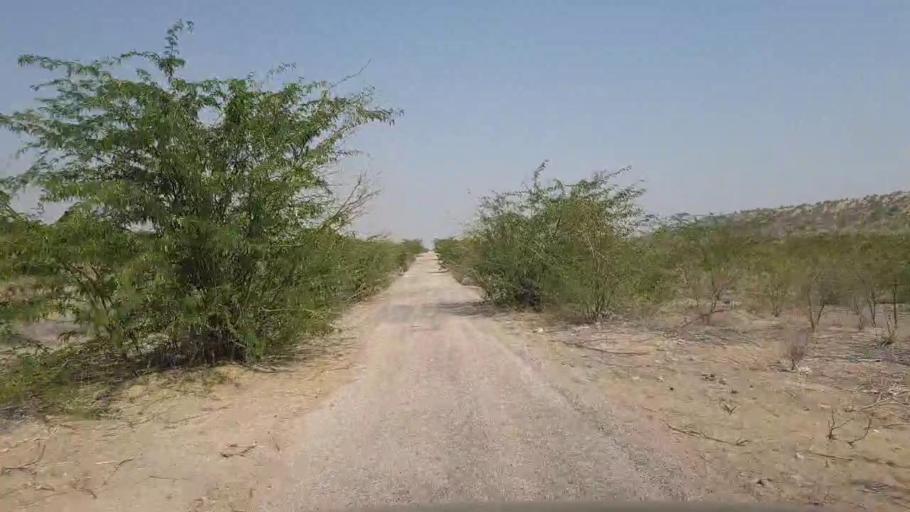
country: PK
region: Sindh
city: Chor
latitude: 25.5870
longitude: 70.1998
